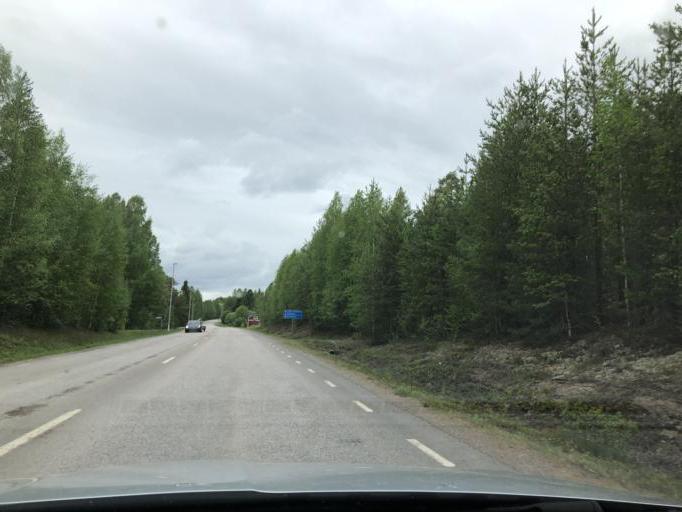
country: SE
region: Norrbotten
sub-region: Pitea Kommun
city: Bergsviken
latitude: 65.3831
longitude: 21.3348
